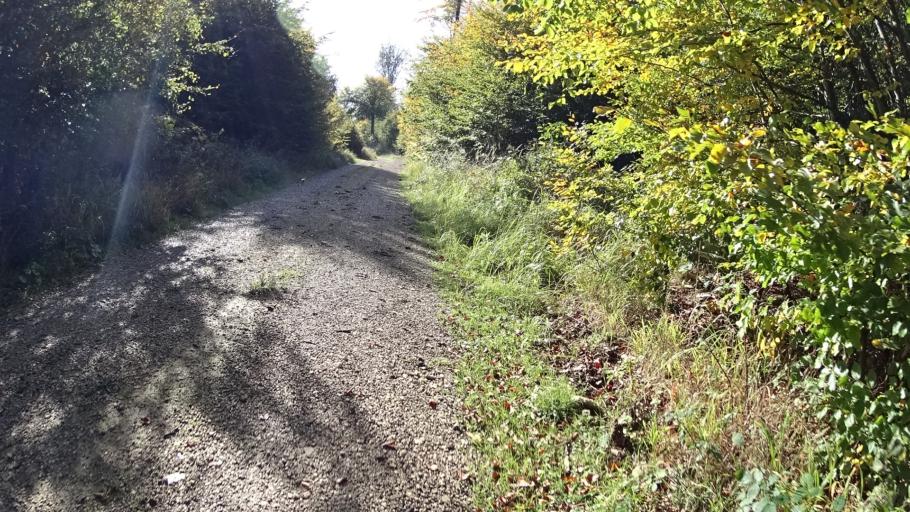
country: DE
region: Bavaria
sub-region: Upper Bavaria
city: Walting
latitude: 48.9028
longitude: 11.3338
